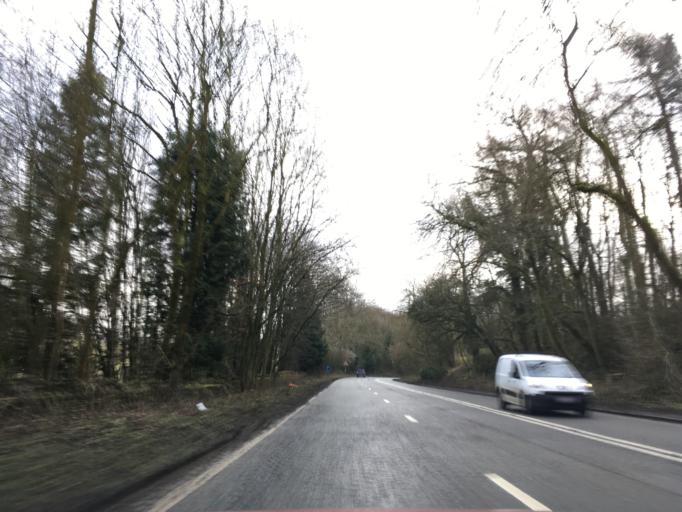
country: GB
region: England
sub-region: Gloucestershire
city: Charlton Kings
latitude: 51.8603
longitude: -2.0489
